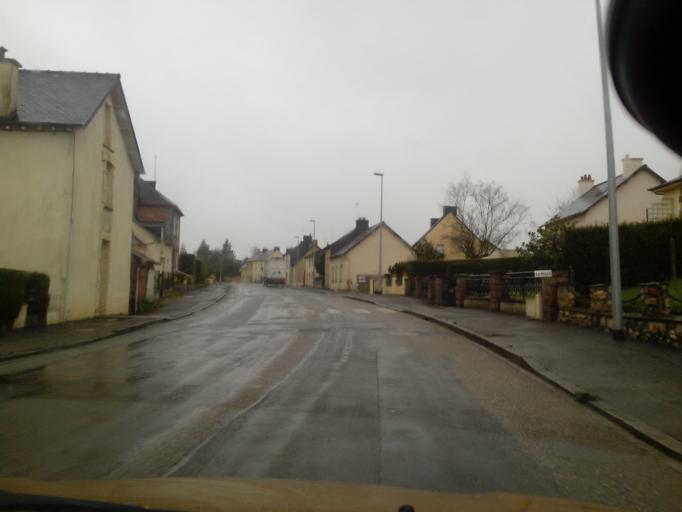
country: FR
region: Brittany
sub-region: Departement d'Ille-et-Vilaine
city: Saint-Meen-le-Grand
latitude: 48.1836
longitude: -2.1979
